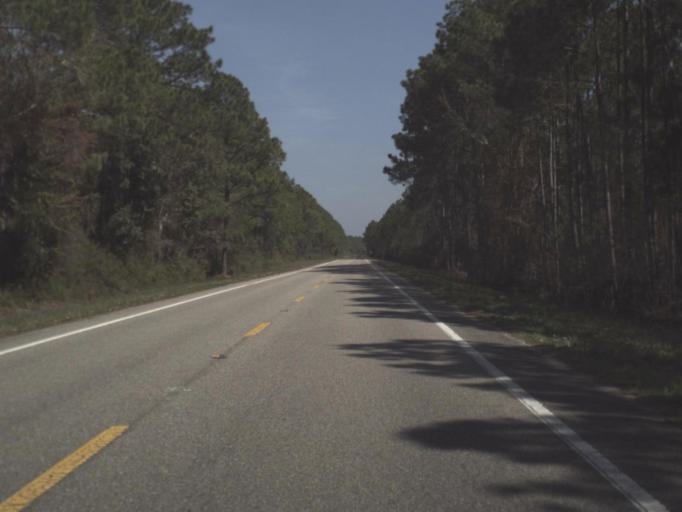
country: US
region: Florida
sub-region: Gulf County
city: Port Saint Joe
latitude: 29.7406
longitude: -85.2057
